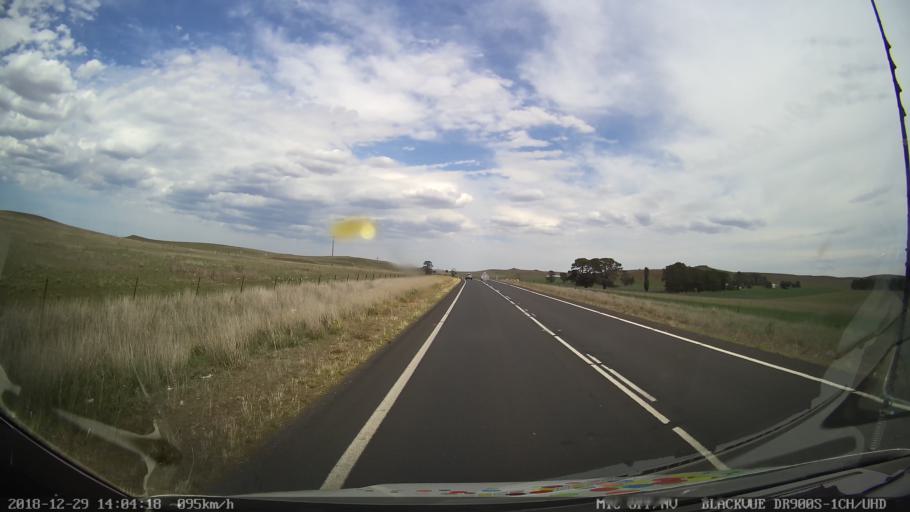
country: AU
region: New South Wales
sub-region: Cooma-Monaro
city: Cooma
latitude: -36.3140
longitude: 149.1862
